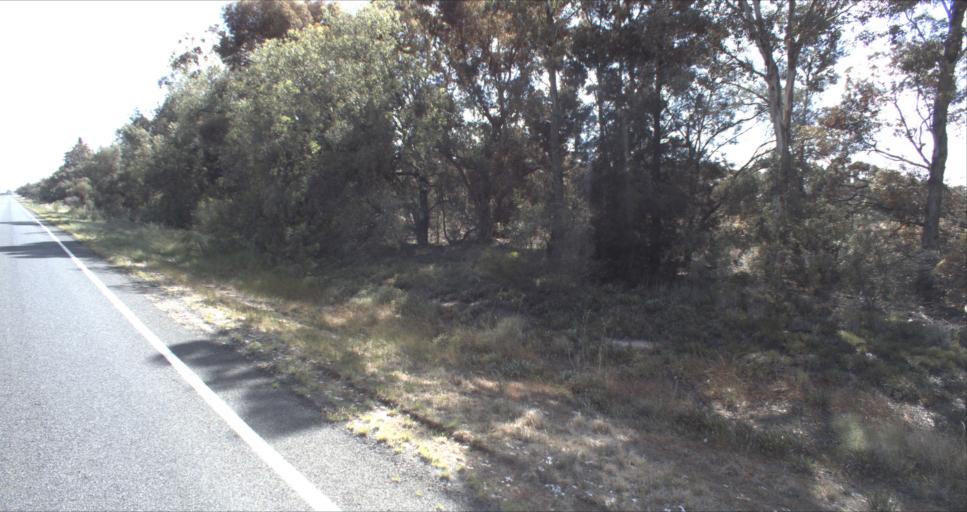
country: AU
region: New South Wales
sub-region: Murrumbidgee Shire
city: Darlington Point
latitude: -34.5307
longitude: 146.1740
